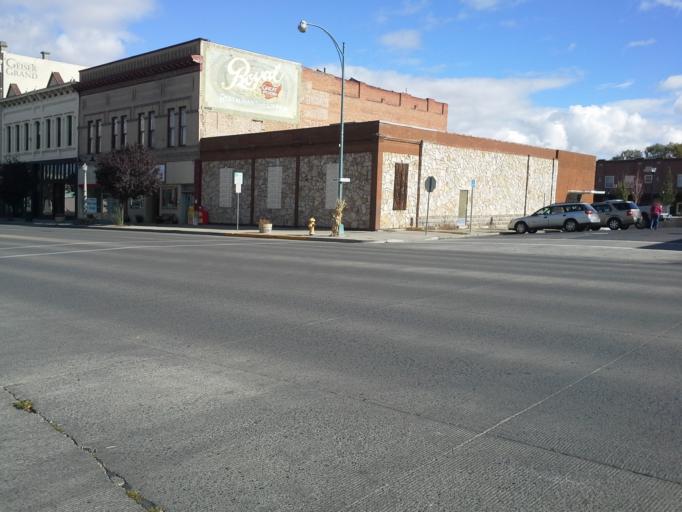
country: US
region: Oregon
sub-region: Baker County
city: Baker City
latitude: 44.7755
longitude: -117.8299
